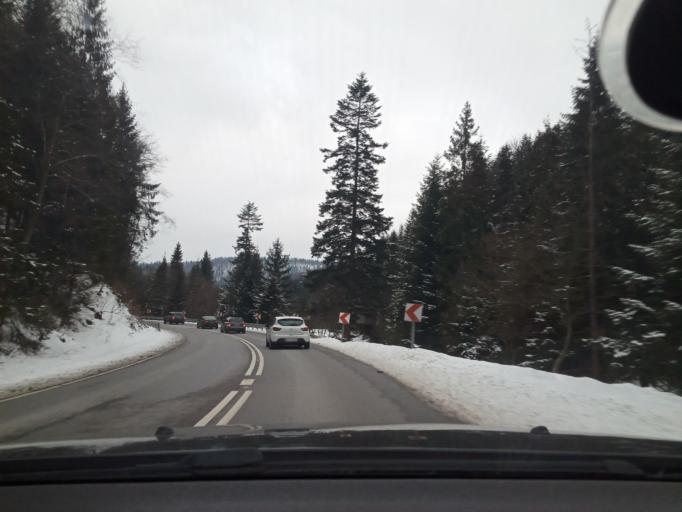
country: PL
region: Lesser Poland Voivodeship
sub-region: Powiat limanowski
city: Lubomierz
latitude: 49.6203
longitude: 20.2432
